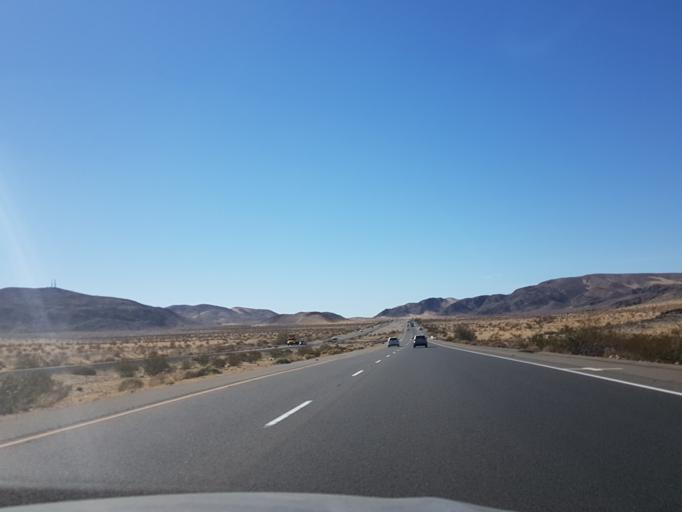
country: US
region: California
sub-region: San Bernardino County
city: Fort Irwin
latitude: 35.0872
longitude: -116.3480
